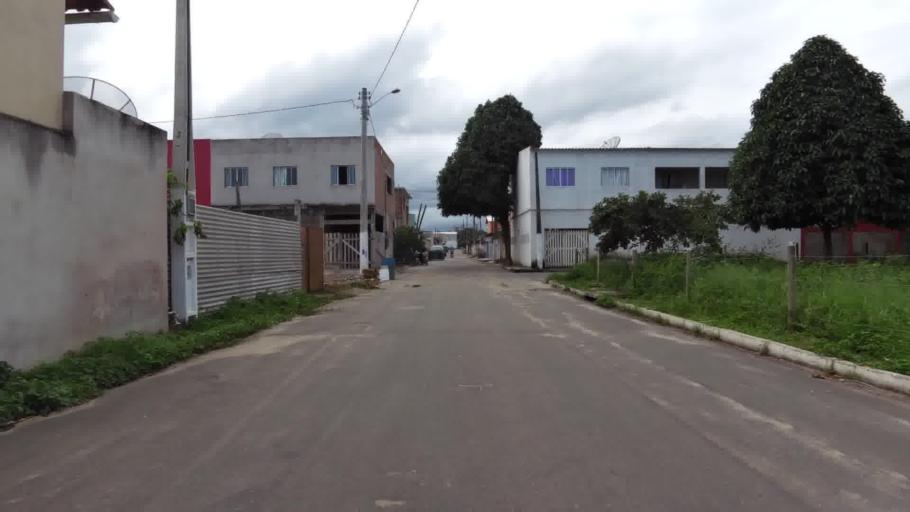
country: BR
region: Espirito Santo
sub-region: Piuma
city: Piuma
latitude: -20.7938
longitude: -40.6390
